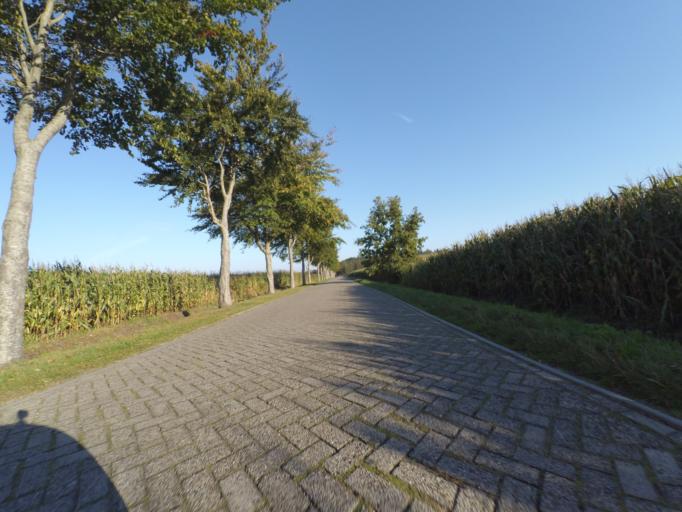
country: NL
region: Gelderland
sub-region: Gemeente Barneveld
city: Voorthuizen
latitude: 52.2058
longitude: 5.5539
